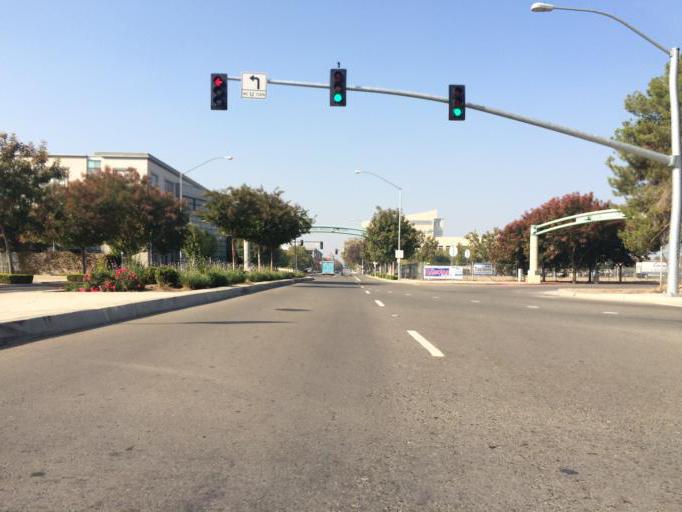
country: US
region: California
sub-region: Fresno County
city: Fresno
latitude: 36.7326
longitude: -119.7796
